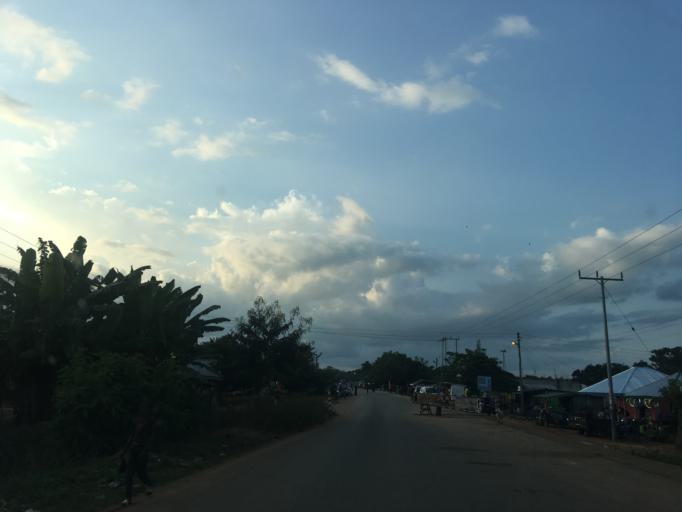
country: GH
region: Western
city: Bibiani
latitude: 6.6492
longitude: -2.4249
